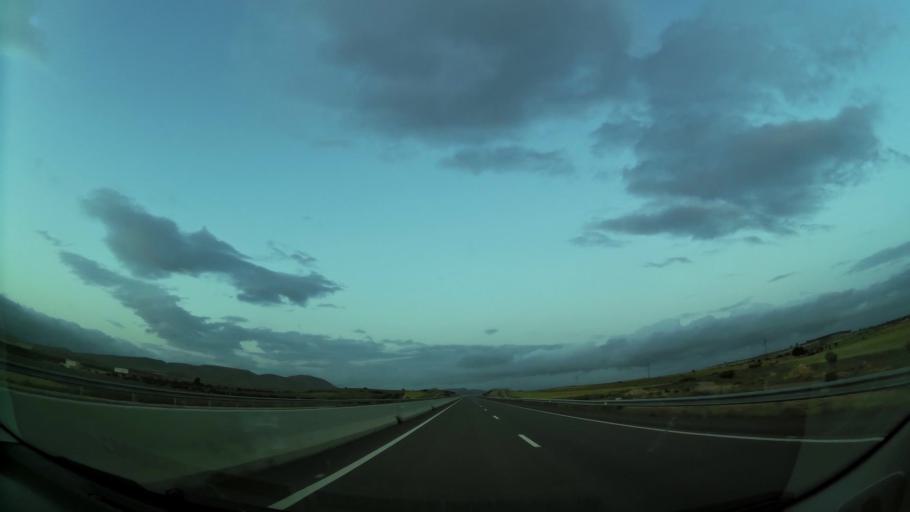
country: MA
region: Oriental
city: El Aioun
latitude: 34.6261
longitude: -2.5168
